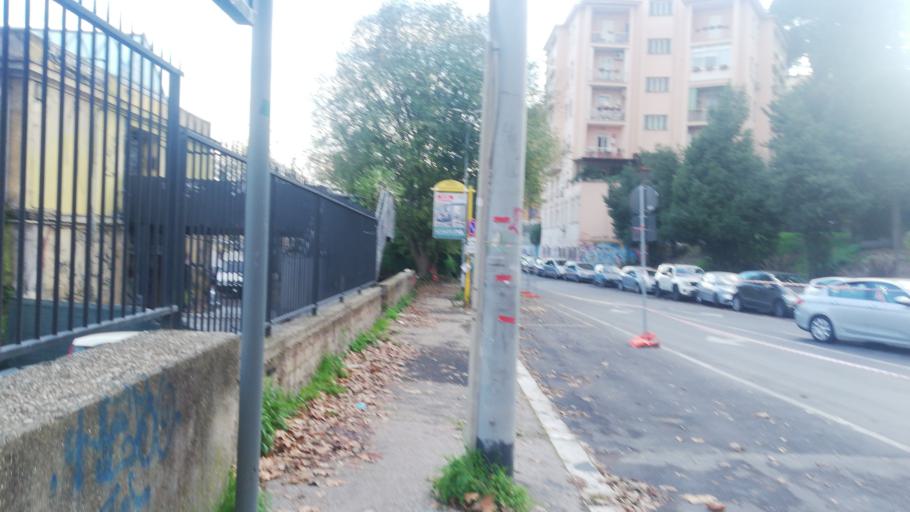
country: IT
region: Latium
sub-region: Citta metropolitana di Roma Capitale
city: Rome
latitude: 41.9329
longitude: 12.5291
